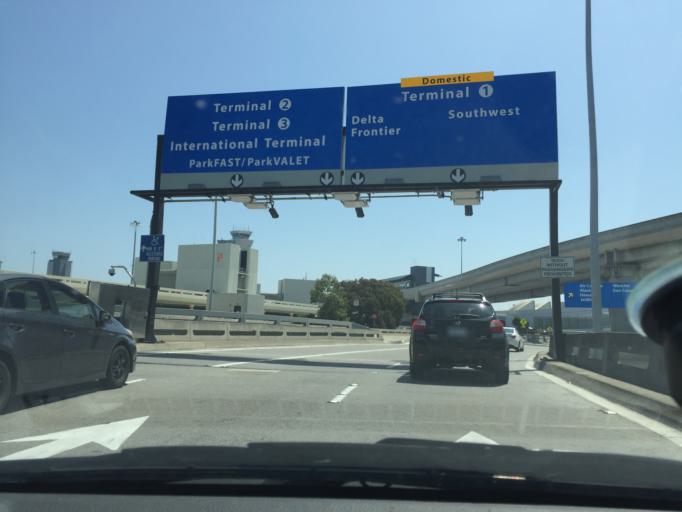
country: US
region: California
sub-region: San Mateo County
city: Millbrae
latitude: 37.6153
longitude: -122.3881
